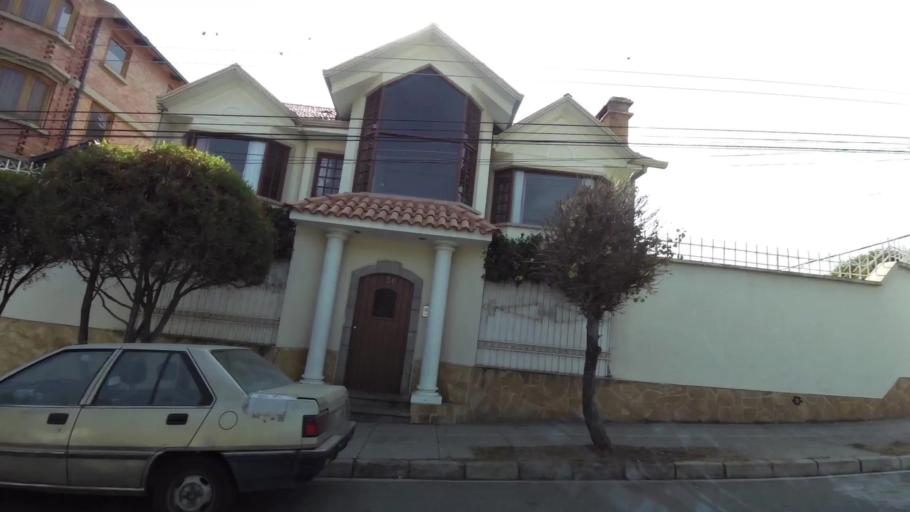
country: BO
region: La Paz
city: La Paz
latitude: -16.5282
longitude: -68.0756
